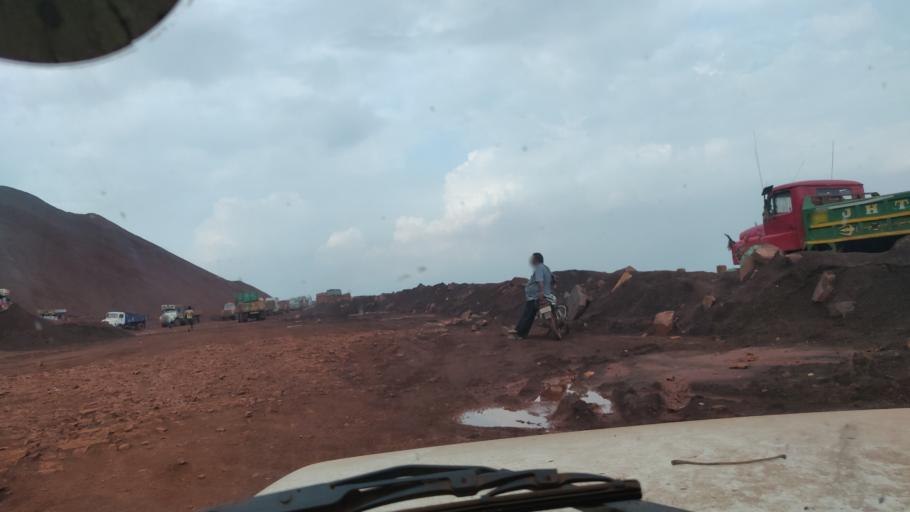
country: IN
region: Odisha
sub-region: Kendujhar
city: Barbil
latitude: 21.6283
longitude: 85.5139
